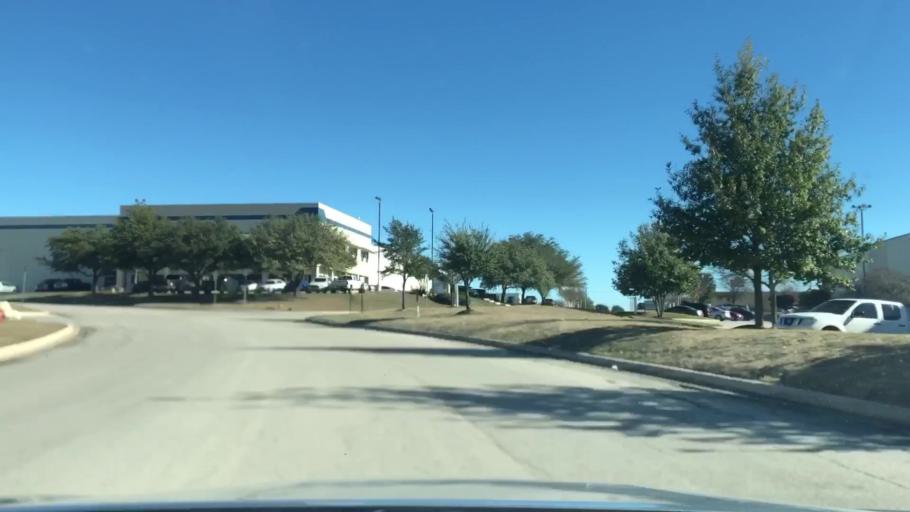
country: US
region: Texas
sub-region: Bexar County
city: Selma
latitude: 29.5999
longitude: -98.2820
